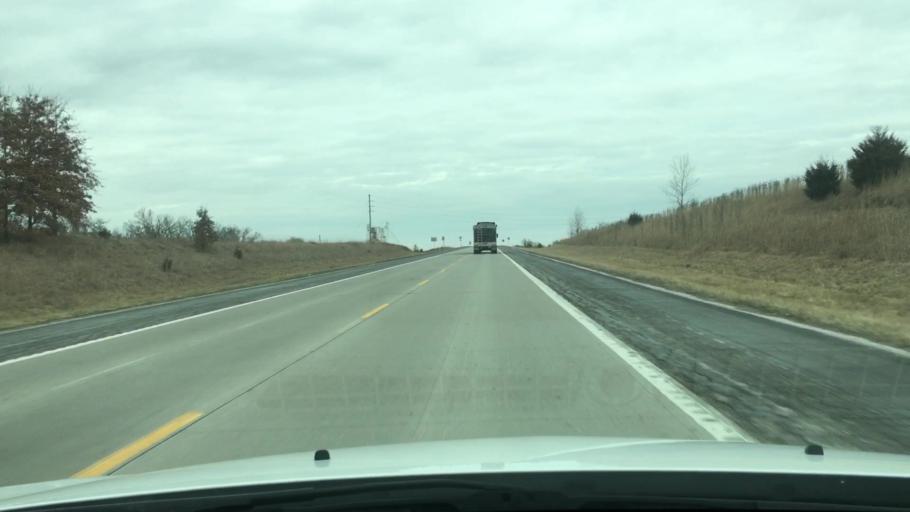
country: US
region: Missouri
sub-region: Audrain County
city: Mexico
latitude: 39.1517
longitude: -91.8435
